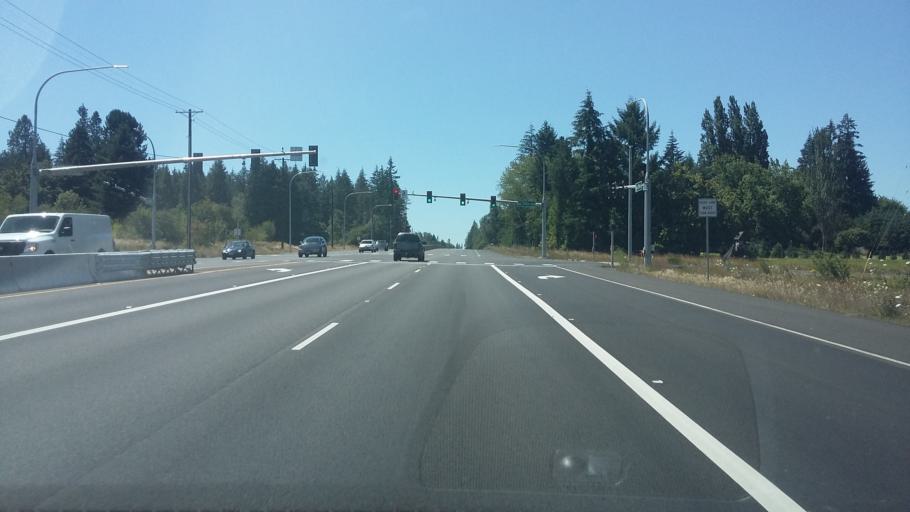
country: US
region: Washington
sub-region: Clark County
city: Dollar Corner
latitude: 45.7800
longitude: -122.6194
